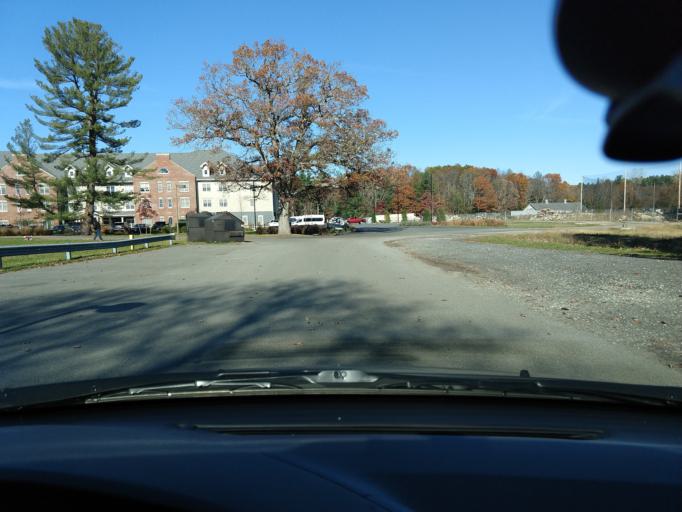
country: US
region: Massachusetts
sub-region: Middlesex County
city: Bedford
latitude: 42.5046
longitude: -71.2700
